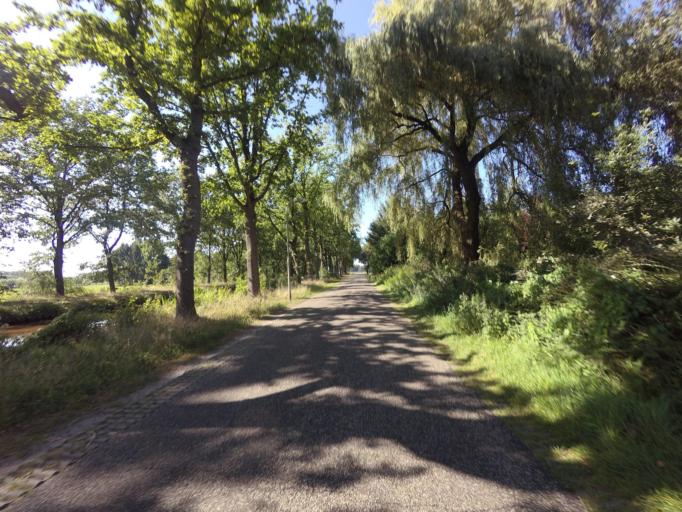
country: NL
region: Overijssel
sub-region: Gemeente Hardenberg
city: Hardenberg
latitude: 52.5347
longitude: 6.6337
